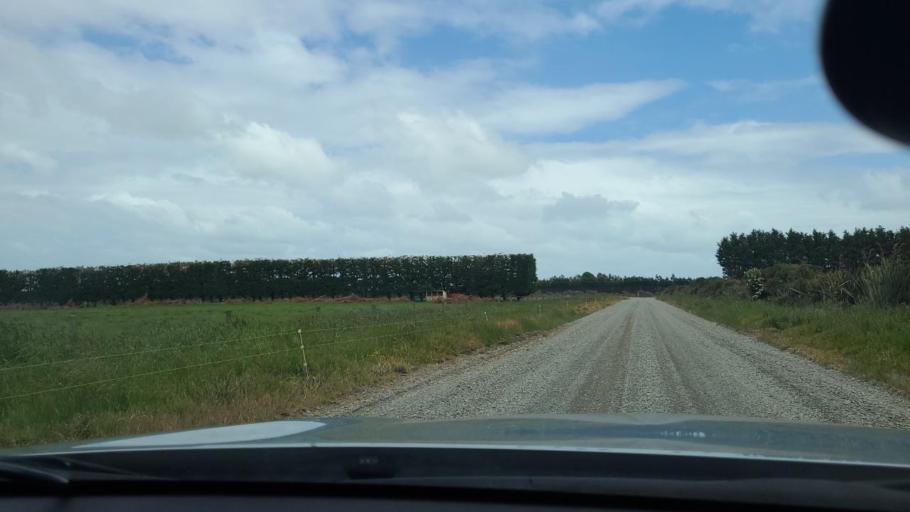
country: NZ
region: Southland
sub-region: Invercargill City
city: Invercargill
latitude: -46.3346
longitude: 168.2354
